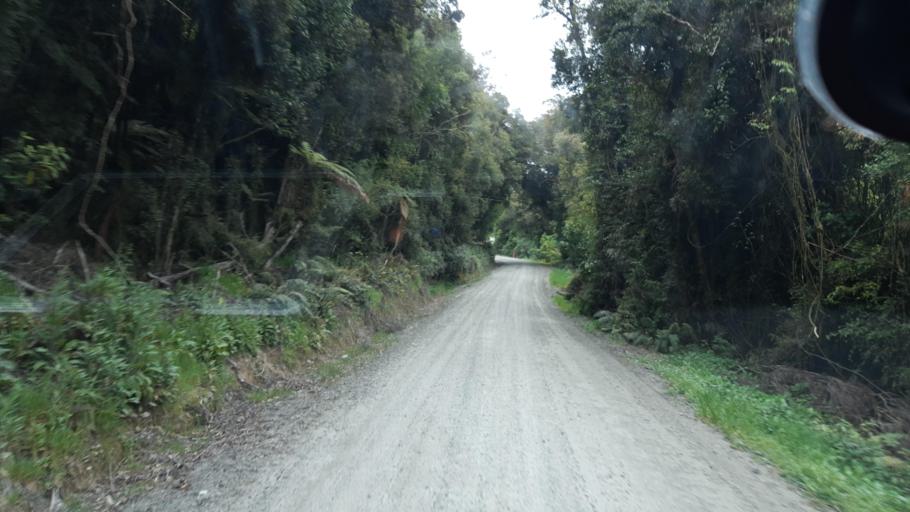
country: NZ
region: West Coast
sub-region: Grey District
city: Greymouth
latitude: -42.6371
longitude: 171.3836
